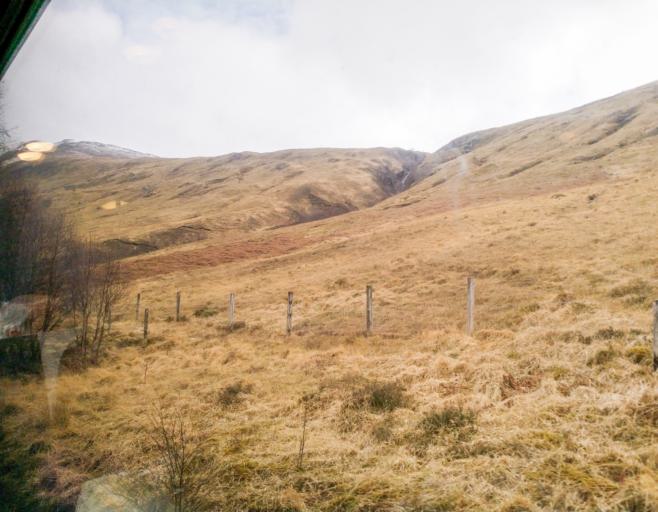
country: GB
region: Scotland
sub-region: Highland
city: Spean Bridge
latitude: 56.8126
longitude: -4.7161
